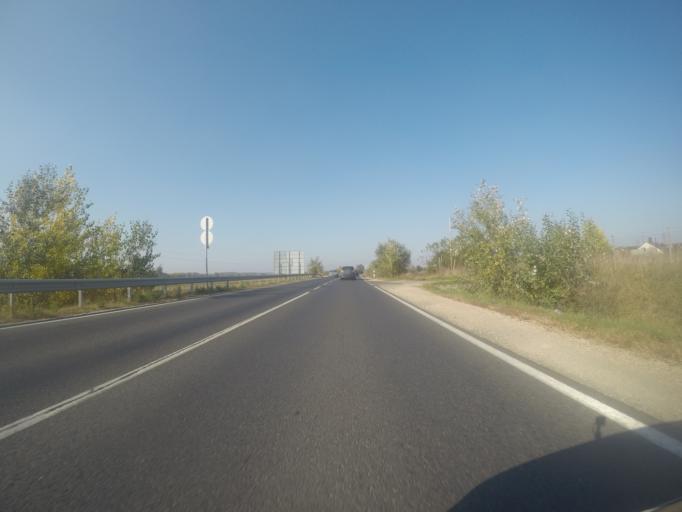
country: HU
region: Tolna
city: Dunafoldvar
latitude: 46.8164
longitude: 18.9073
